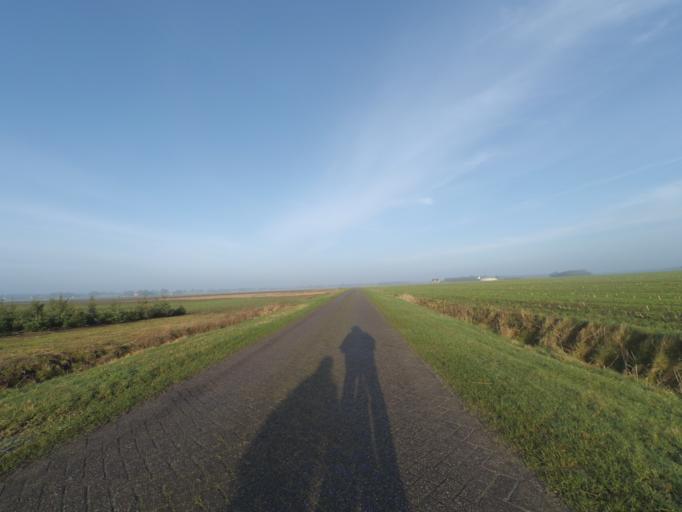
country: NL
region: Drenthe
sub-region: Gemeente Borger-Odoorn
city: Borger
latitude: 52.8864
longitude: 6.8027
